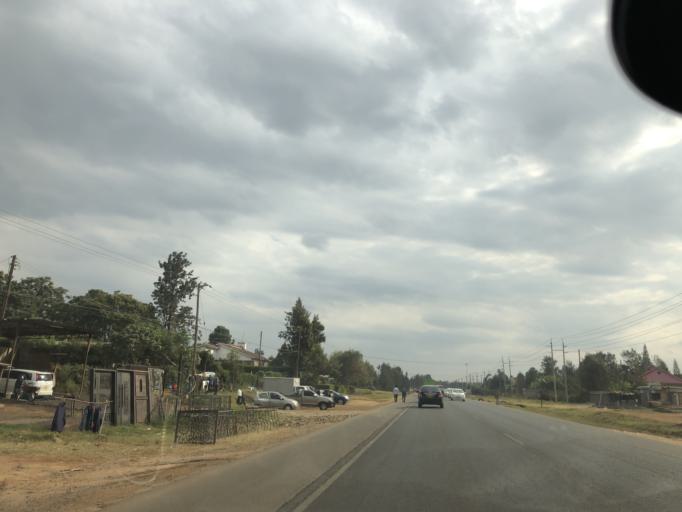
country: KE
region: Kiambu
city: Kiambu
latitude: -1.2125
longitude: 36.8721
